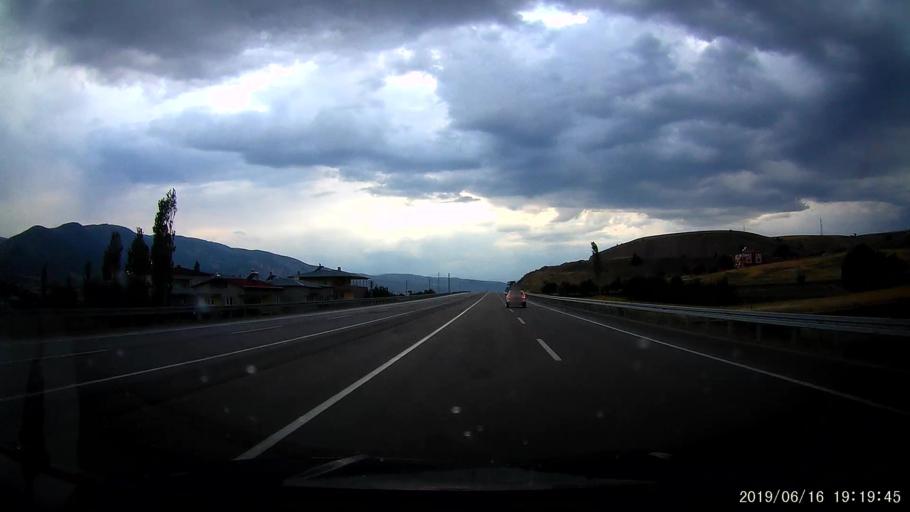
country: TR
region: Sivas
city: Akincilar
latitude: 40.0949
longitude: 38.4196
